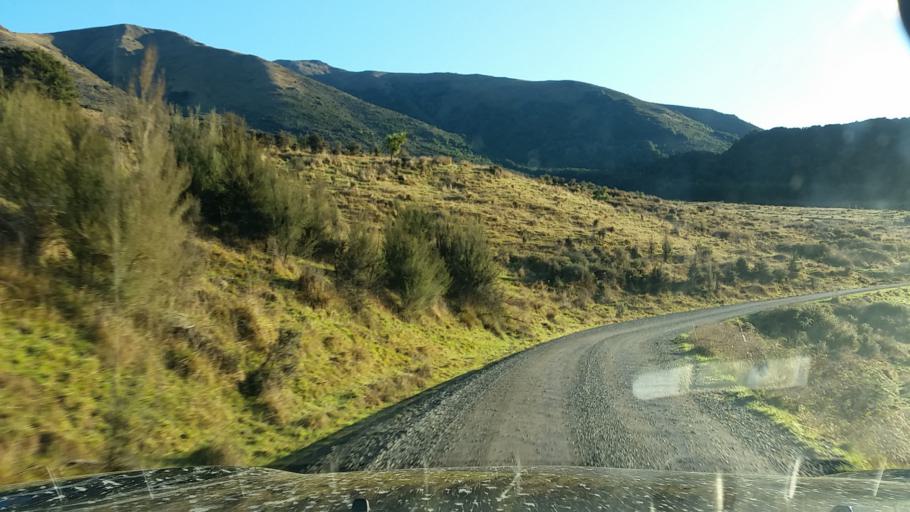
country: NZ
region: Marlborough
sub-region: Marlborough District
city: Blenheim
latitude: -41.7909
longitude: 173.7857
